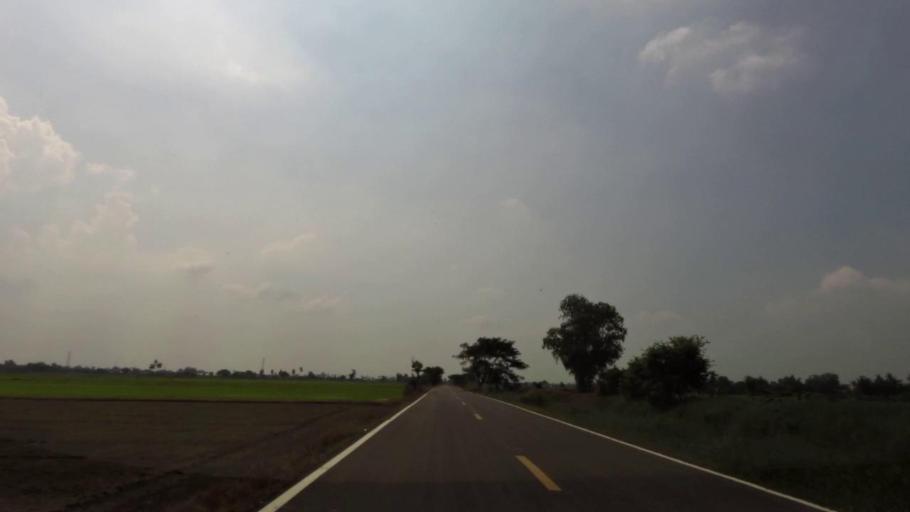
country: TH
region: Ang Thong
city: Pho Thong
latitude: 14.6276
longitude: 100.4053
